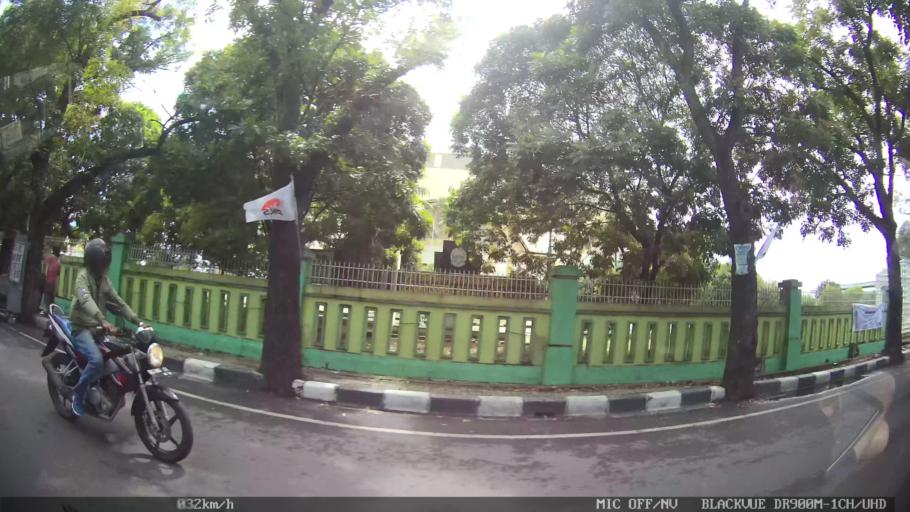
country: ID
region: North Sumatra
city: Medan
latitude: 3.6080
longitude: 98.7070
